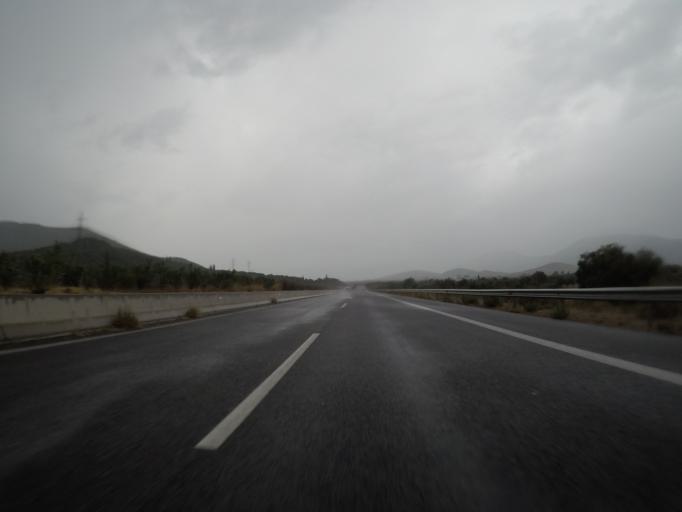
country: GR
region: Peloponnese
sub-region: Nomos Messinias
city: Meligalas
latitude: 37.2238
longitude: 22.0083
